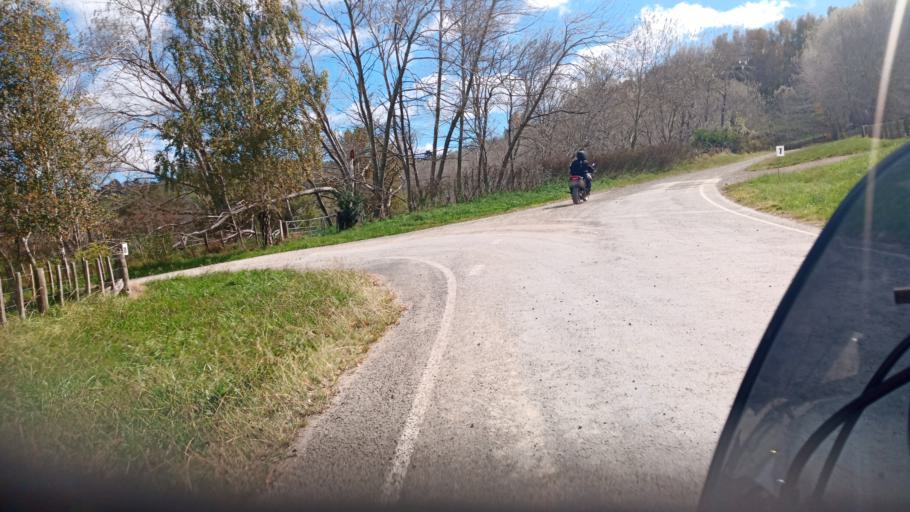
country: NZ
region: Gisborne
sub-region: Gisborne District
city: Gisborne
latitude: -38.4254
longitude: 177.7237
